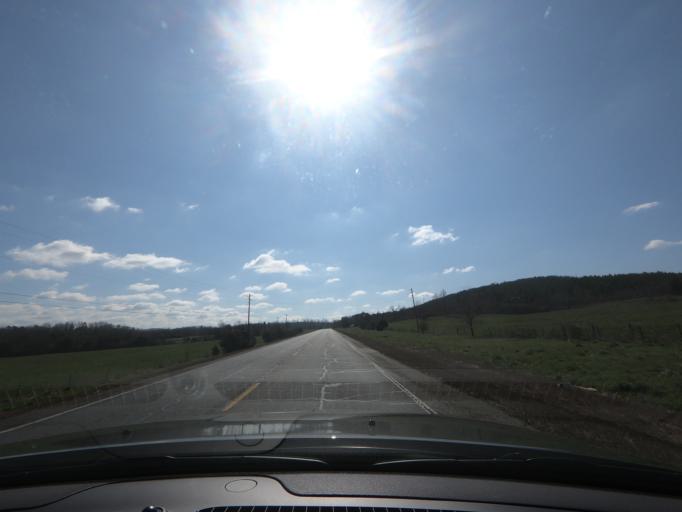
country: US
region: Georgia
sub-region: Bartow County
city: Rydal
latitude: 34.3656
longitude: -84.7145
